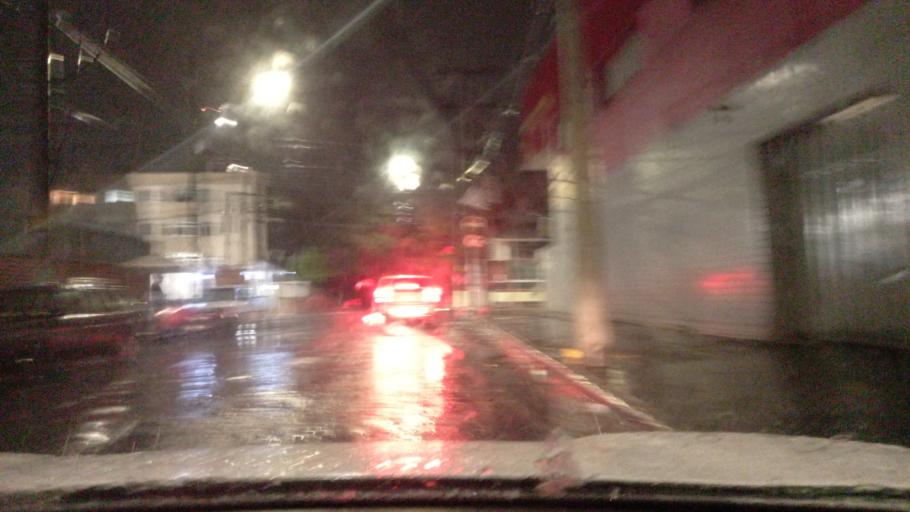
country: BR
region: Minas Gerais
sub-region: Belo Horizonte
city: Belo Horizonte
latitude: -19.9038
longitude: -43.9777
